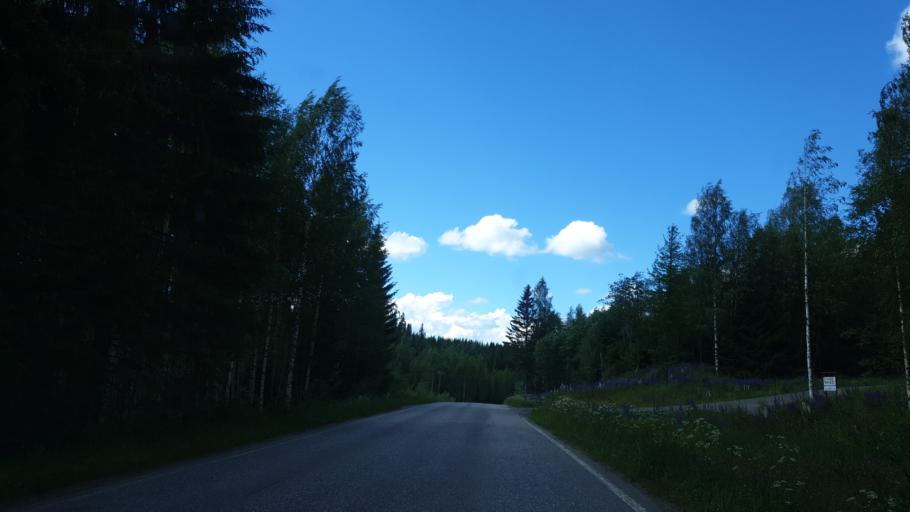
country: FI
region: Northern Savo
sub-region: Koillis-Savo
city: Kaavi
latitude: 63.0269
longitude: 28.6178
